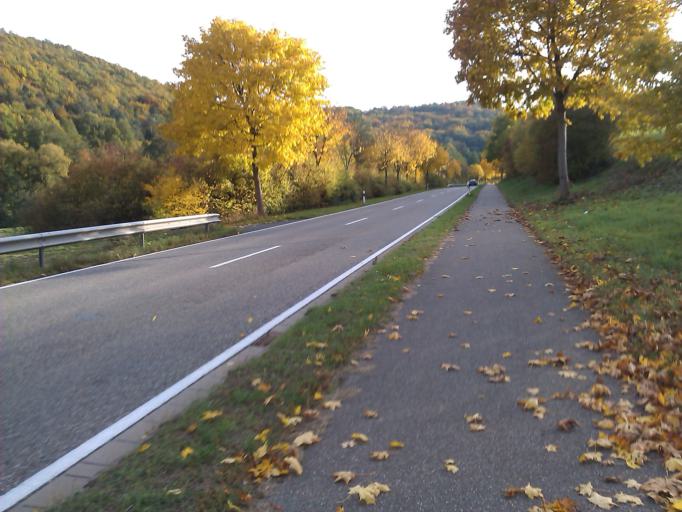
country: DE
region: Rheinland-Pfalz
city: Niederkirchen
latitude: 49.5690
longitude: 7.6932
